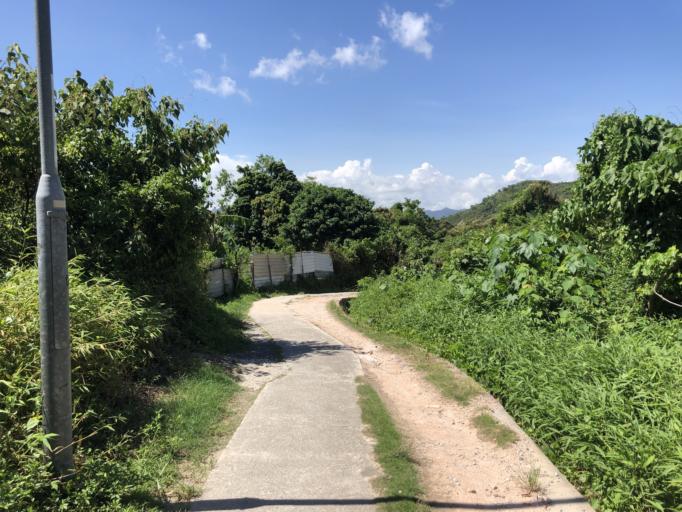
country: HK
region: Tuen Mun
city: Tuen Mun
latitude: 22.2905
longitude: 113.9788
